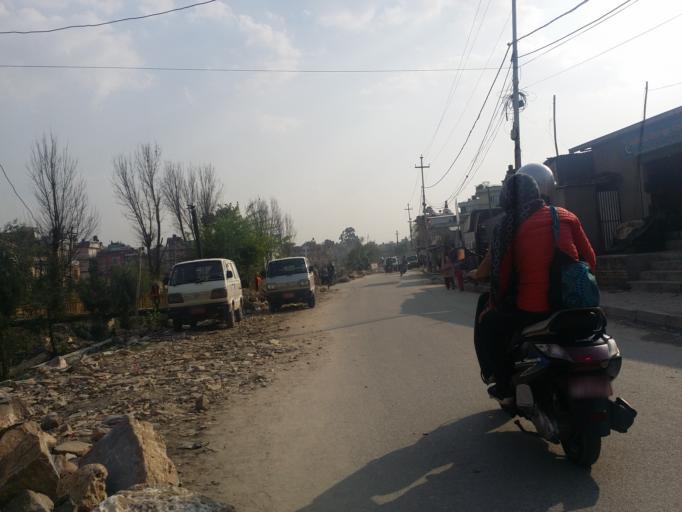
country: NP
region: Central Region
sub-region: Bagmati Zone
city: Kathmandu
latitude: 27.7006
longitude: 85.3484
